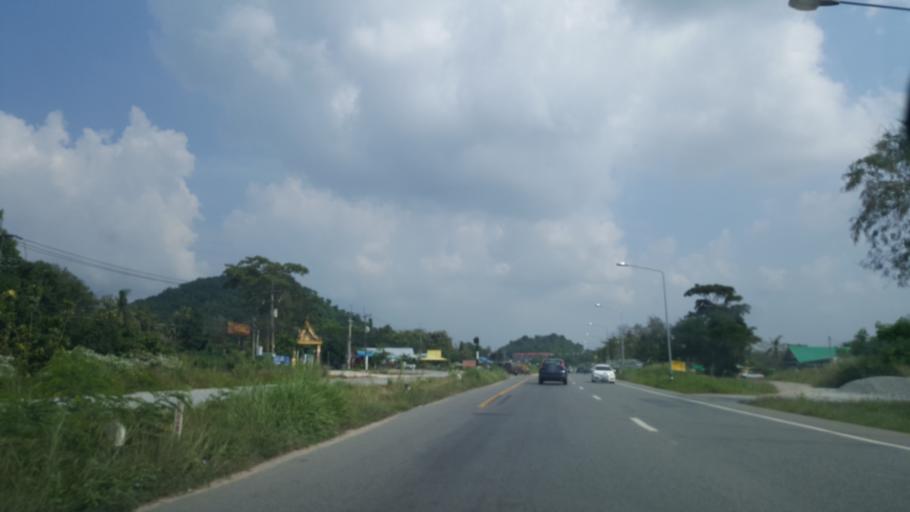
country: TH
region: Rayong
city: Ban Chang
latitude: 12.7348
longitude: 100.9877
